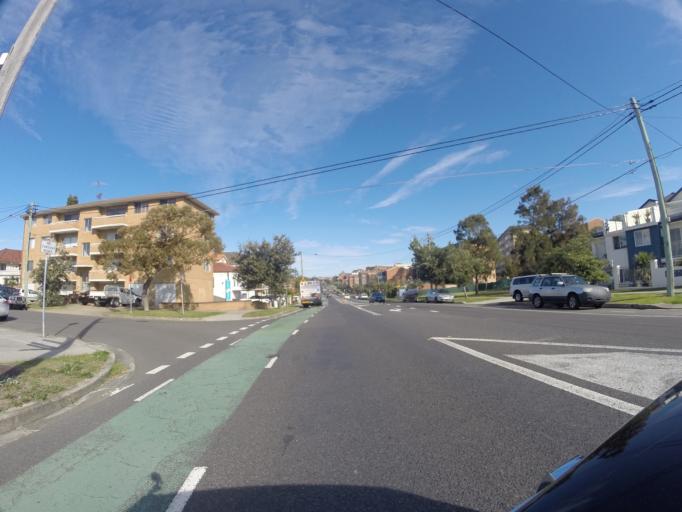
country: AU
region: New South Wales
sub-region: Randwick
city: South Coogee
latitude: -33.9347
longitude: 151.2581
